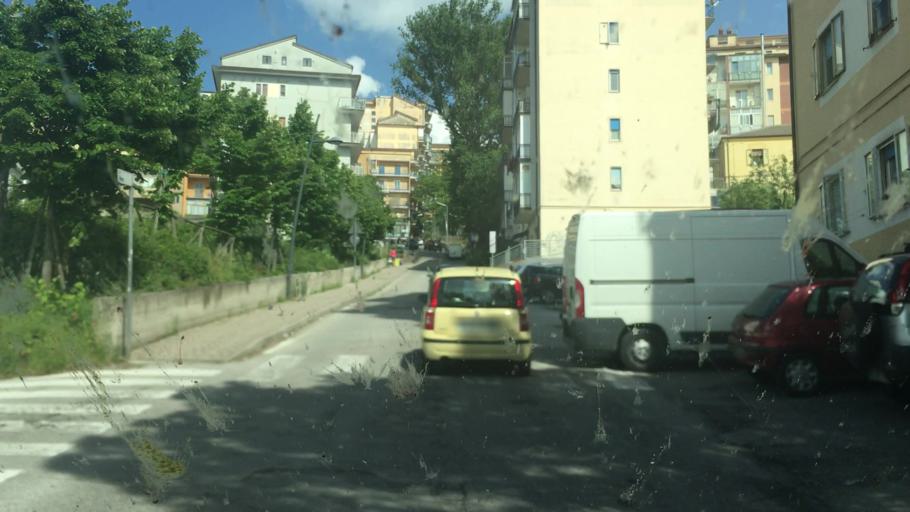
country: IT
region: Basilicate
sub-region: Provincia di Potenza
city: Potenza
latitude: 40.6423
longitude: 15.8019
